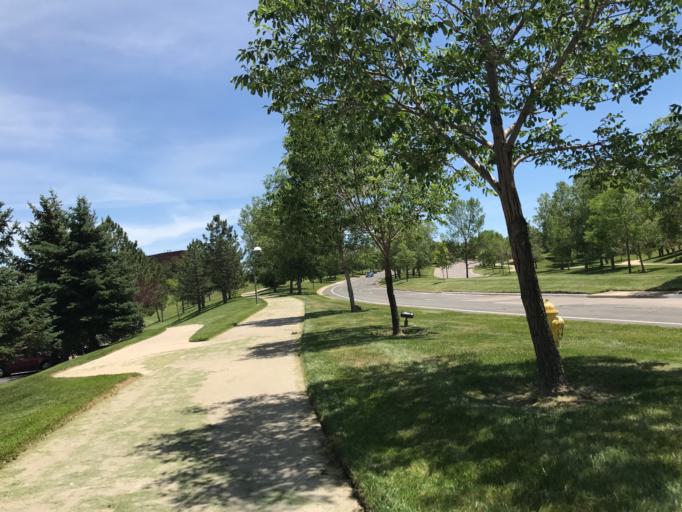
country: US
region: Colorado
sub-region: Broomfield County
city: Broomfield
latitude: 39.9226
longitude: -105.1133
